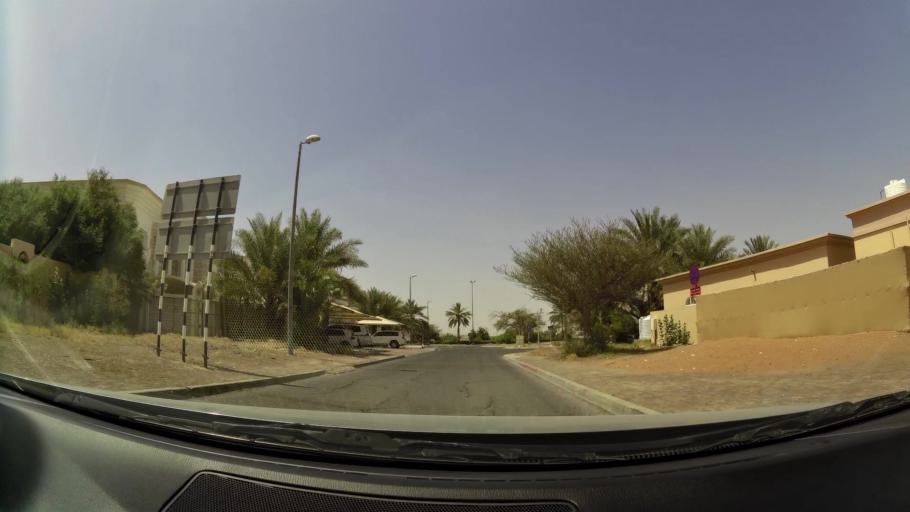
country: OM
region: Al Buraimi
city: Al Buraymi
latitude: 24.2757
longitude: 55.7757
